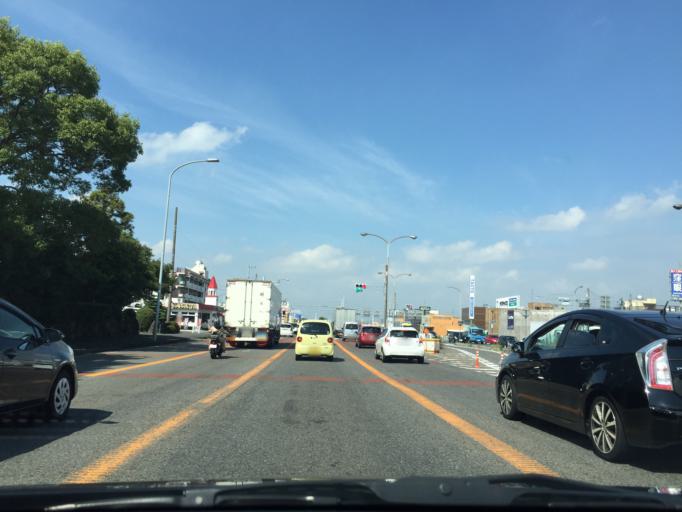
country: JP
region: Gifu
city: Kasamatsucho
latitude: 35.3882
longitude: 136.7556
